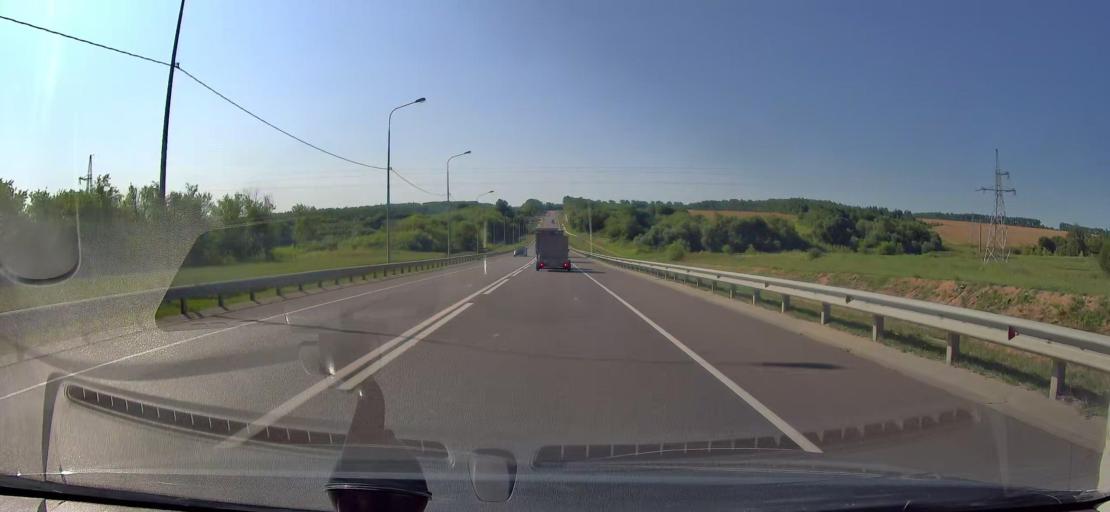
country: RU
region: Orjol
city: Kromy
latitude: 52.6234
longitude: 35.7577
